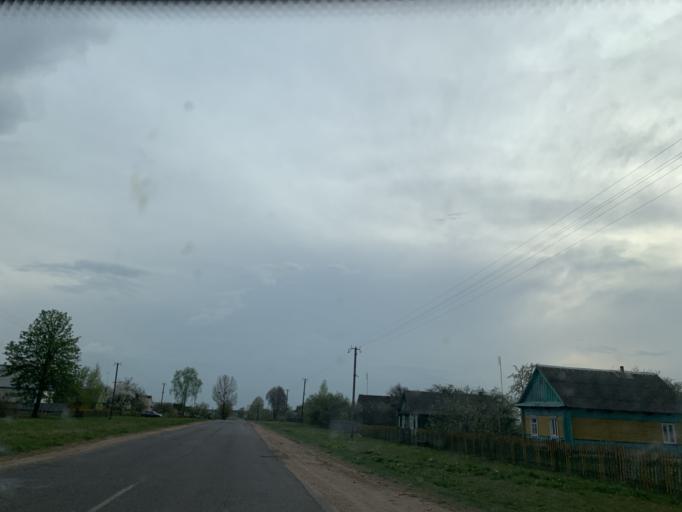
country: BY
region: Minsk
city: Kapyl'
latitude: 53.2735
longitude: 26.9666
